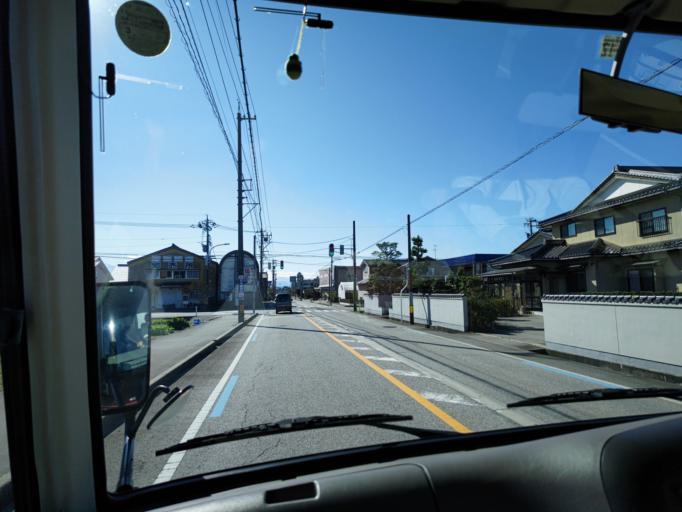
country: JP
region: Toyama
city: Nyuzen
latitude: 36.8954
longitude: 137.4194
